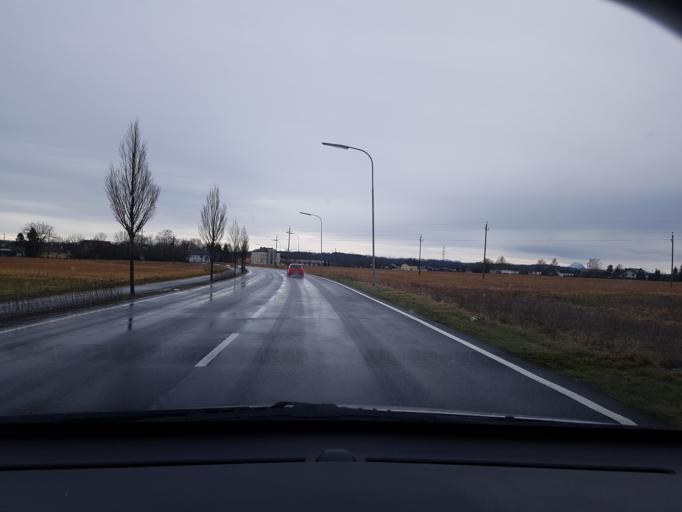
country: AT
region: Upper Austria
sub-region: Politischer Bezirk Linz-Land
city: Traun
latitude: 48.2191
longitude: 14.2189
